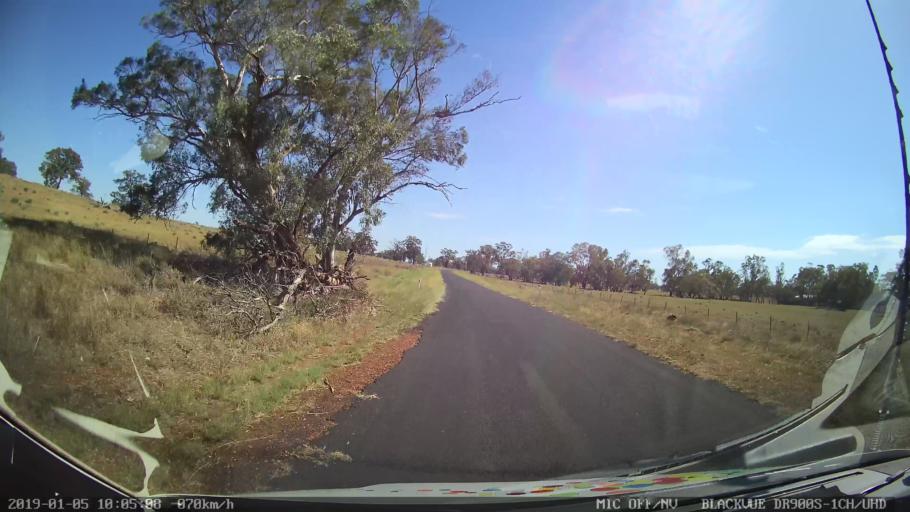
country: AU
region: New South Wales
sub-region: Gilgandra
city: Gilgandra
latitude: -31.6691
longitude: 148.8640
